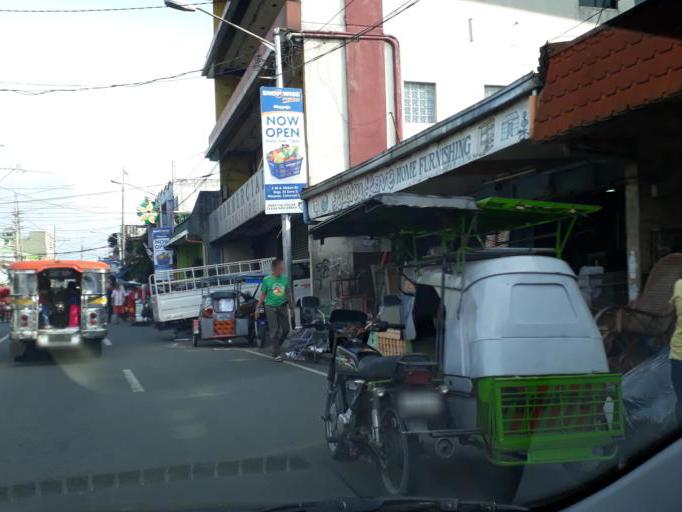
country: PH
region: Metro Manila
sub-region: Caloocan City
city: Niugan
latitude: 14.6445
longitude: 120.9741
